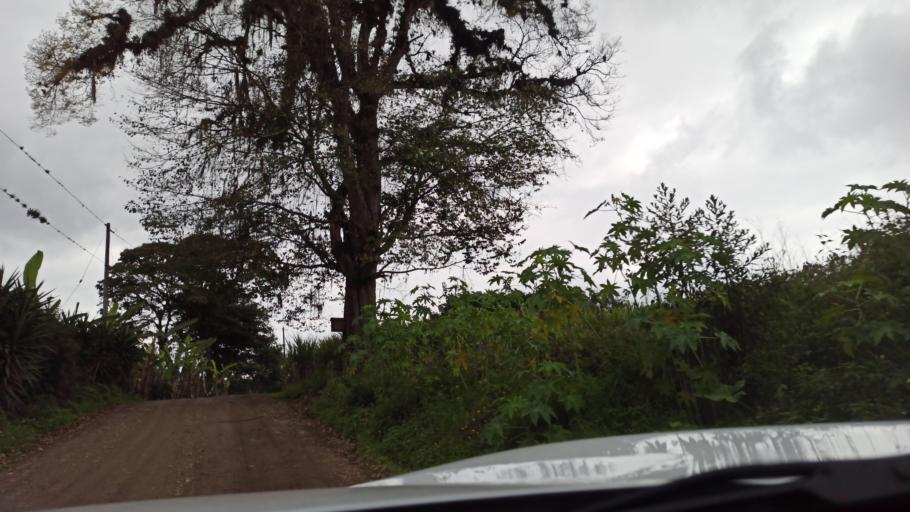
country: MX
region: Veracruz
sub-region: Chocaman
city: San Jose Neria
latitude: 18.9849
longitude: -97.0067
